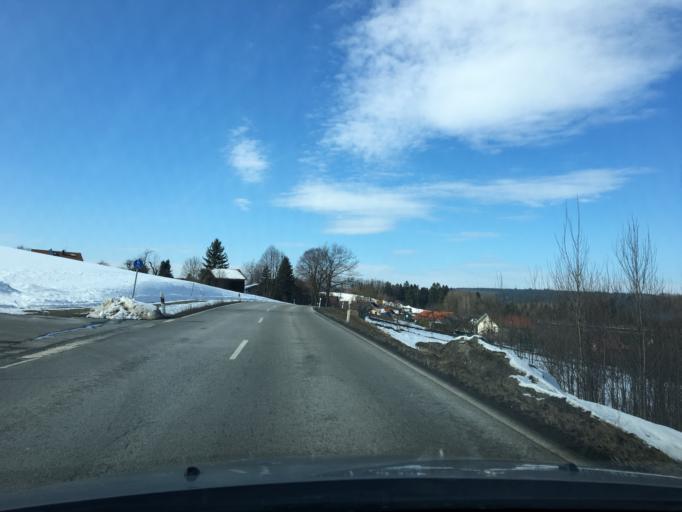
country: DE
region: Bavaria
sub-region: Lower Bavaria
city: Freyung
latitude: 48.8075
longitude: 13.5351
